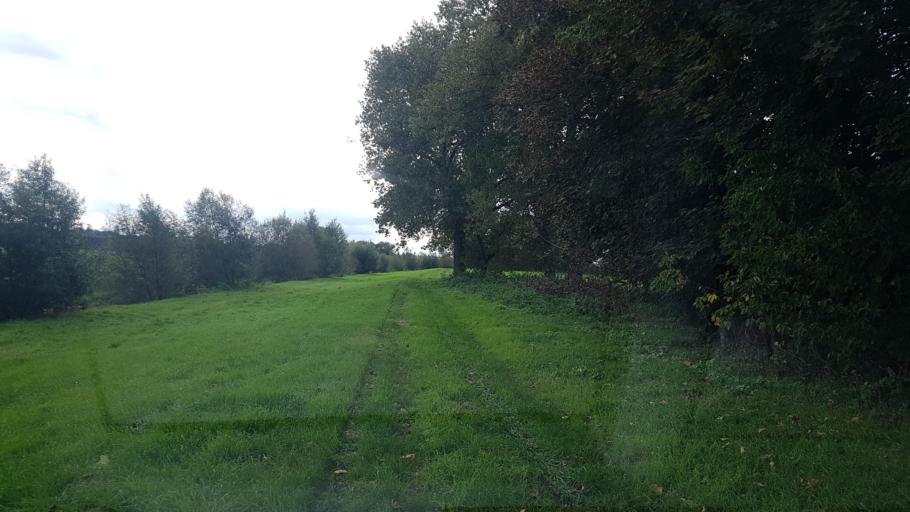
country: DE
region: Saxony
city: Pegau
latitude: 51.1538
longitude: 12.2622
